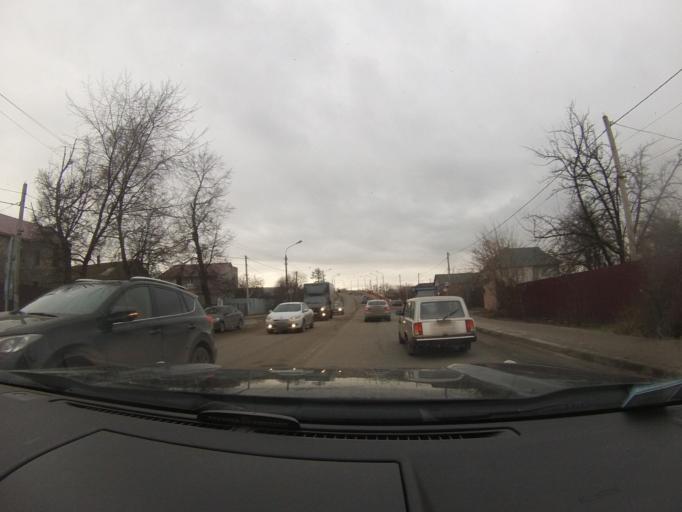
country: RU
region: Moskovskaya
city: Lopatinskiy
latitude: 55.3261
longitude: 38.6904
